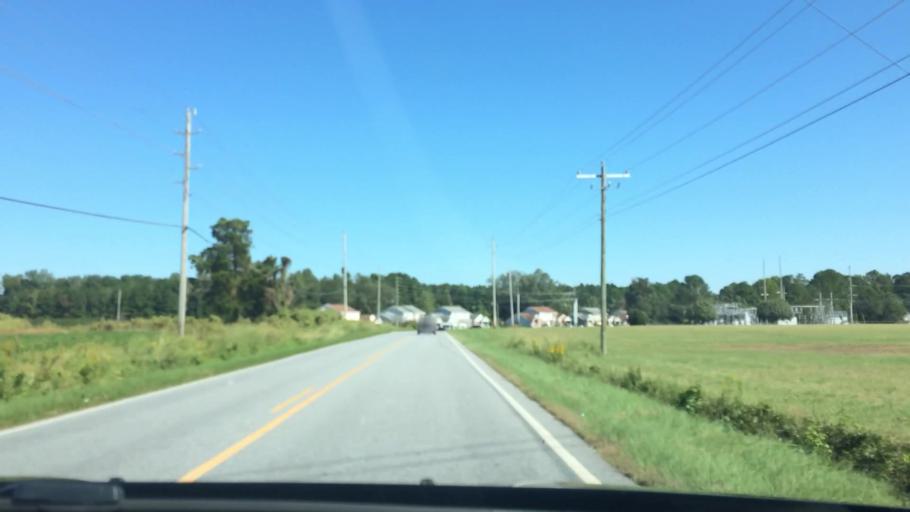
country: US
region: North Carolina
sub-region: Pitt County
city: Summerfield
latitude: 35.6157
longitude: -77.4241
